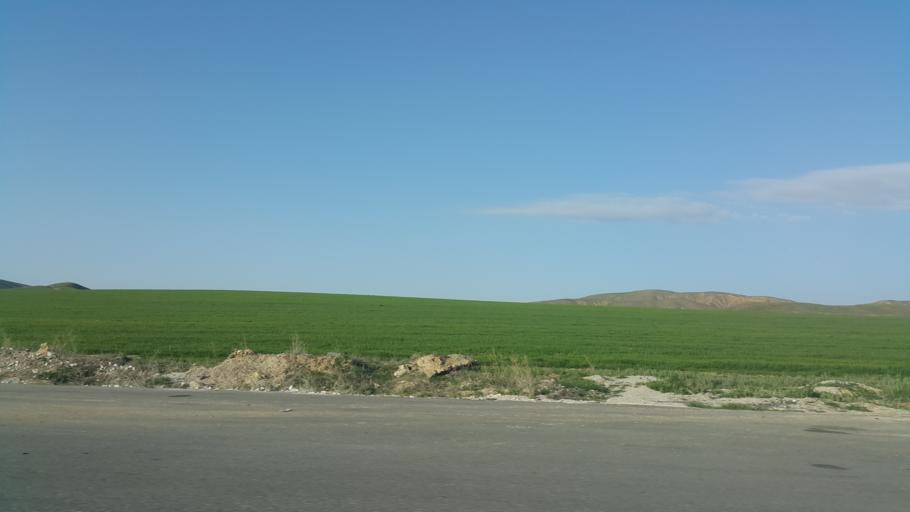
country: TR
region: Ankara
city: Sereflikochisar
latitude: 39.1122
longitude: 33.3641
